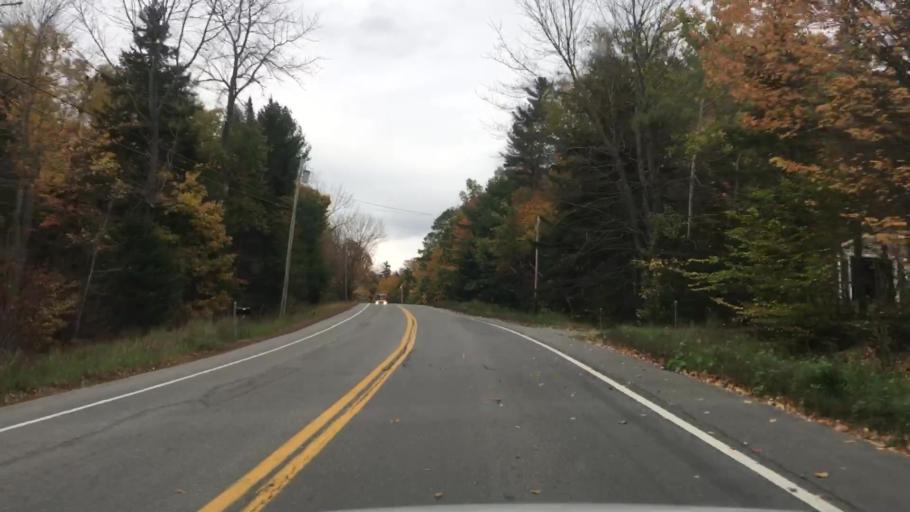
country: US
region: Maine
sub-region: Hancock County
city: Bucksport
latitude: 44.5600
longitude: -68.8463
